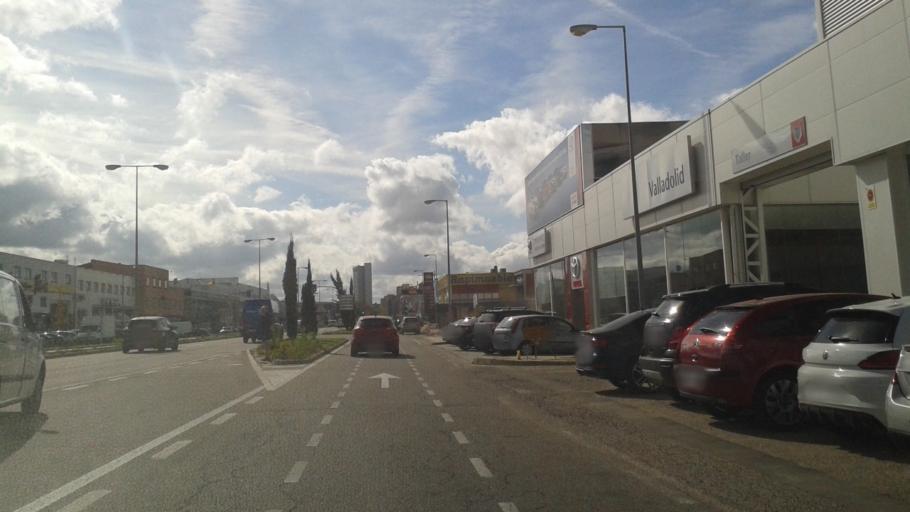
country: ES
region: Castille and Leon
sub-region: Provincia de Valladolid
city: Valladolid
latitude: 41.6694
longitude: -4.7272
